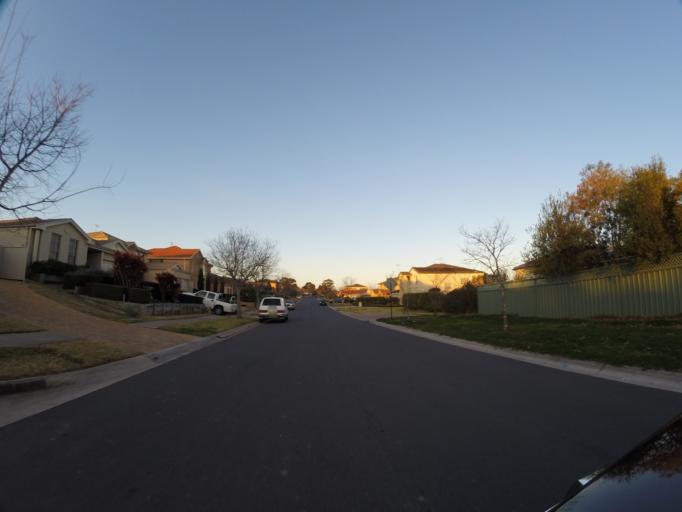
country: AU
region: New South Wales
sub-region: Camden
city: Narellan
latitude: -34.0238
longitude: 150.7296
